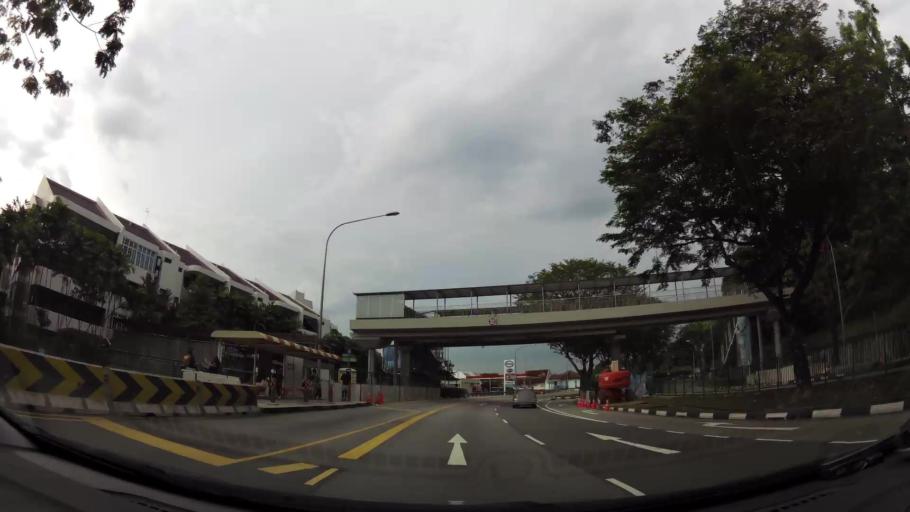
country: SG
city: Singapore
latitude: 1.3570
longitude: 103.8291
